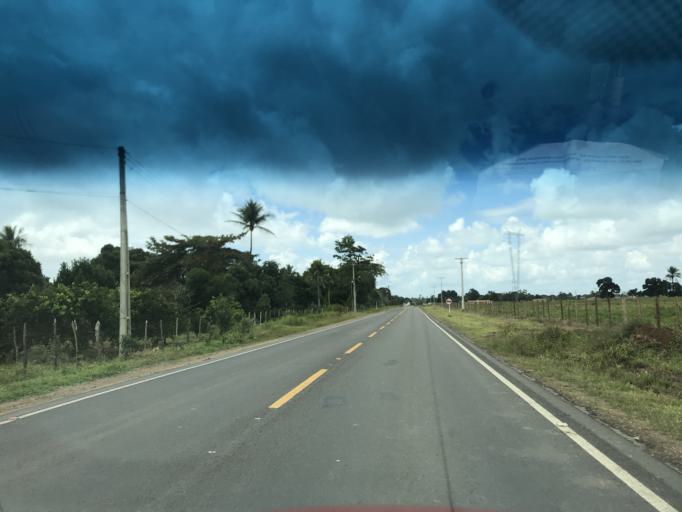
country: BR
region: Bahia
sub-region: Conceicao Do Almeida
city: Conceicao do Almeida
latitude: -12.7233
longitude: -39.2084
